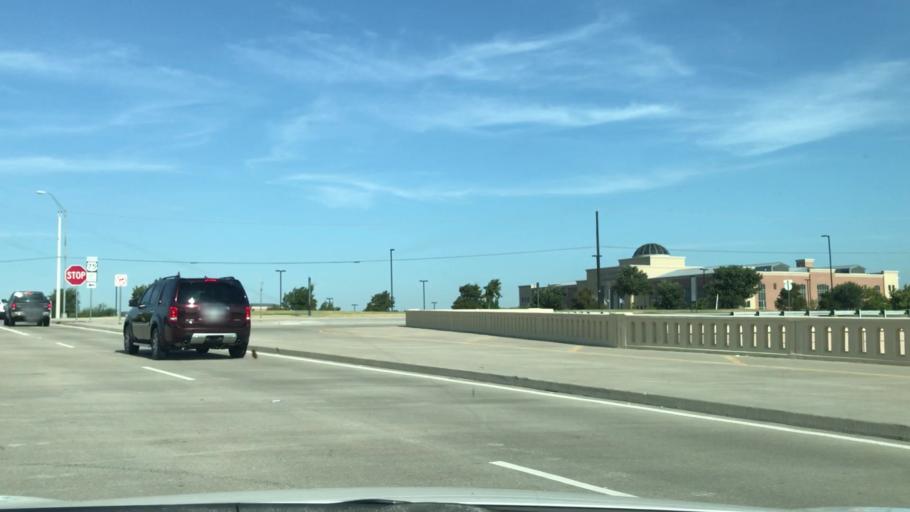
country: US
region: Texas
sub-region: Collin County
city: McKinney
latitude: 33.2399
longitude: -96.6295
